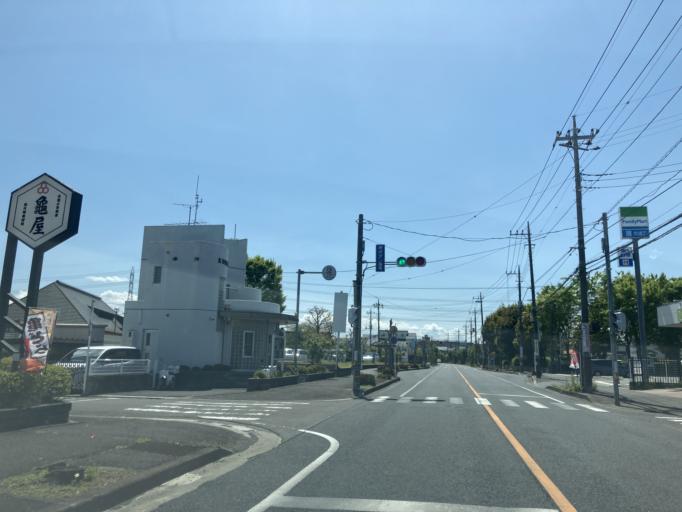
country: JP
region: Saitama
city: Sayama
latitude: 35.8821
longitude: 139.4113
